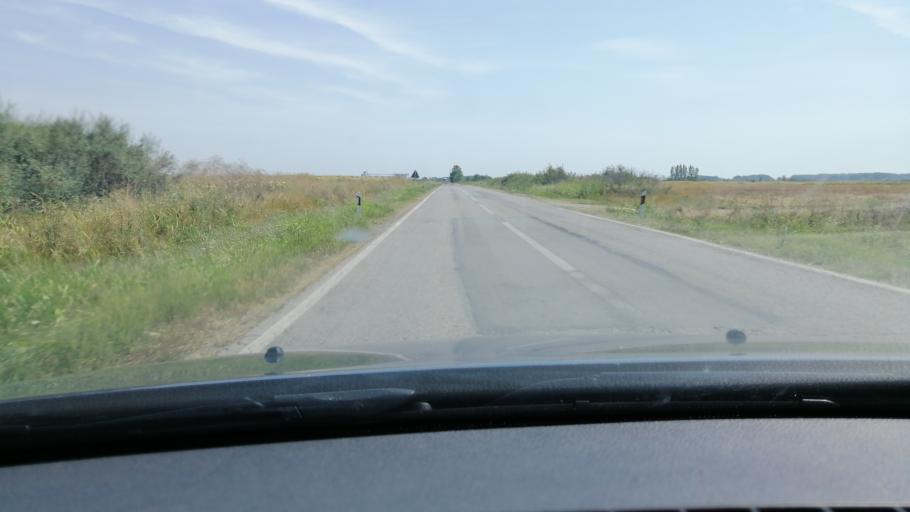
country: RS
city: Neuzina
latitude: 45.3764
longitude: 20.7343
